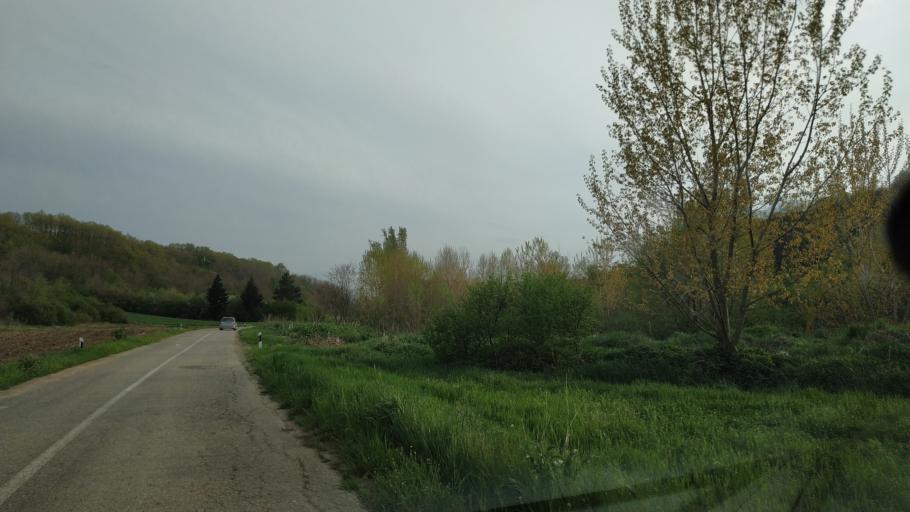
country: RS
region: Central Serbia
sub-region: Nisavski Okrug
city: Aleksinac
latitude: 43.4626
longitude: 21.8036
